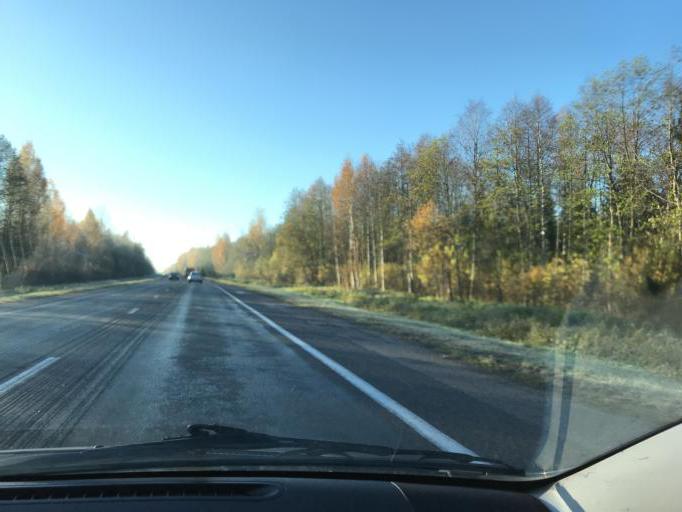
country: BY
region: Vitebsk
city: Vitebsk
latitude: 54.9572
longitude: 30.3573
